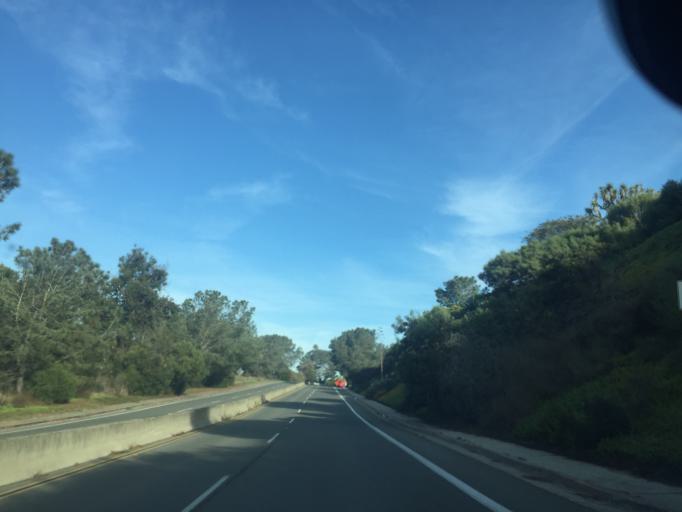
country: US
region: California
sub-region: San Diego County
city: La Jolla
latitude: 32.8623
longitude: -117.2428
